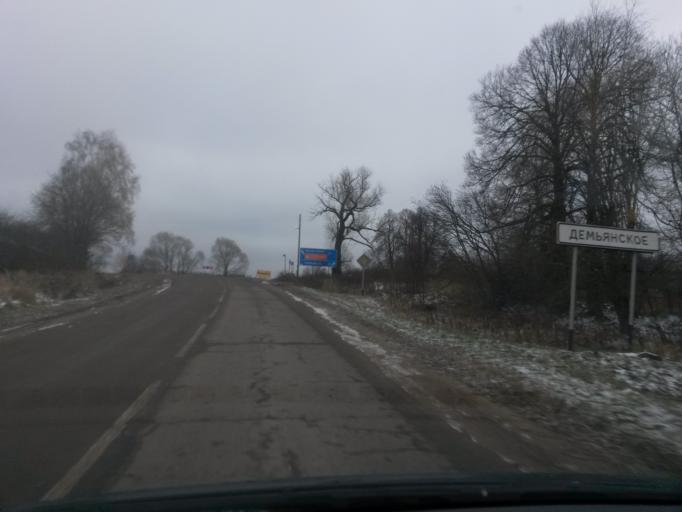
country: RU
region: Jaroslavl
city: Petrovsk
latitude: 56.9665
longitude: 39.3035
